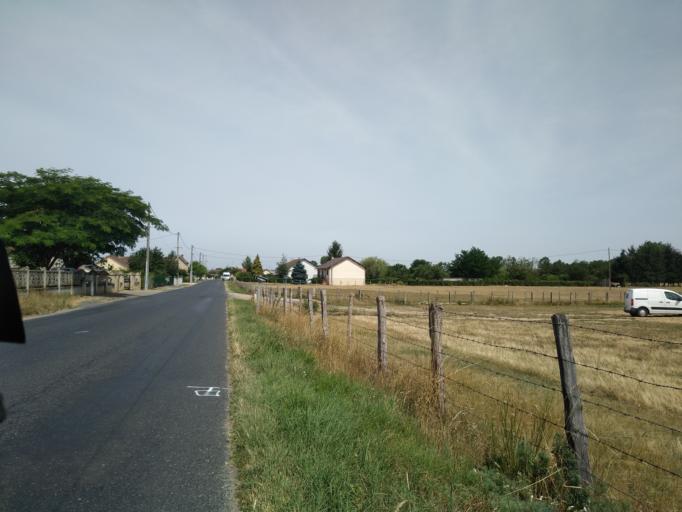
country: FR
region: Bourgogne
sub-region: Departement de Saone-et-Loire
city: Digoin
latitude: 46.4492
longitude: 3.9700
